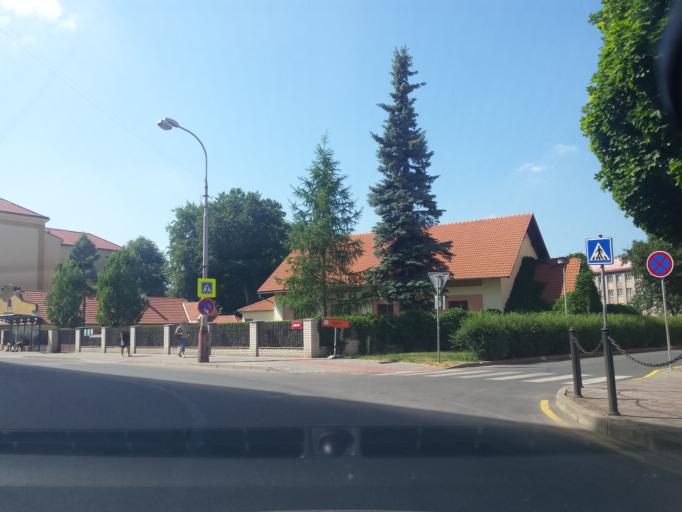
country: CZ
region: Central Bohemia
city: Kralupy nad Vltavou
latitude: 50.2412
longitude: 14.3129
